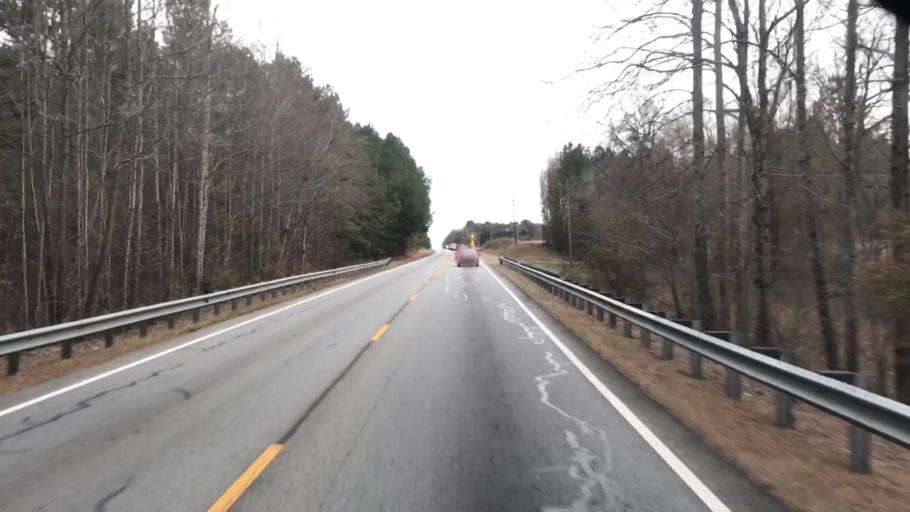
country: US
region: Georgia
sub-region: Jackson County
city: Hoschton
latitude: 34.0731
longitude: -83.7886
